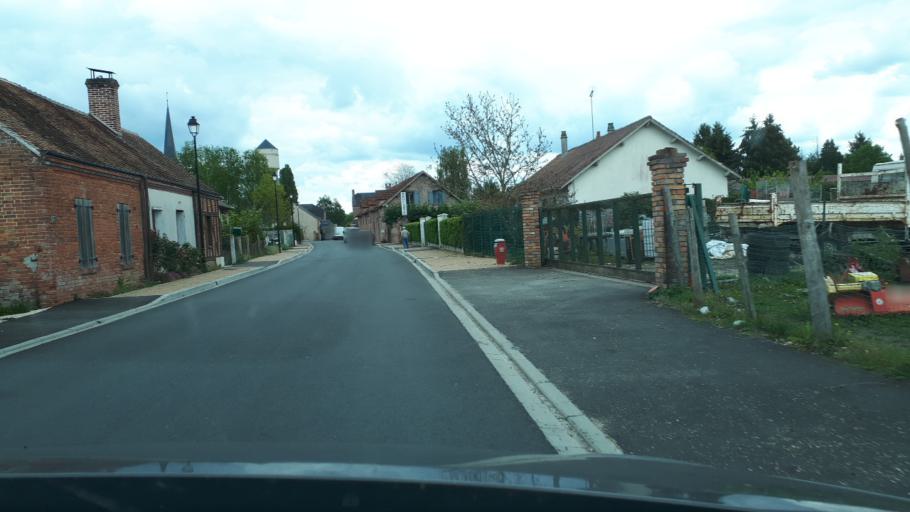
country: FR
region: Centre
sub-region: Departement du Loir-et-Cher
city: Saint-Viatre
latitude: 47.5225
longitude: 1.9303
